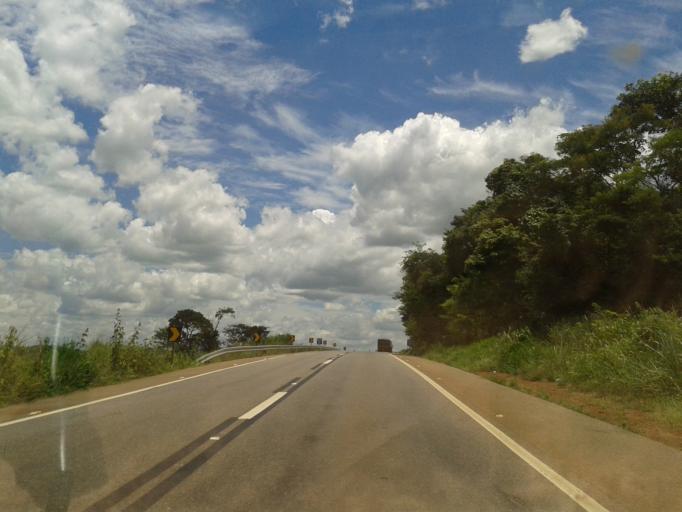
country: BR
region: Goias
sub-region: Neropolis
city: Neropolis
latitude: -16.3219
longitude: -49.2632
